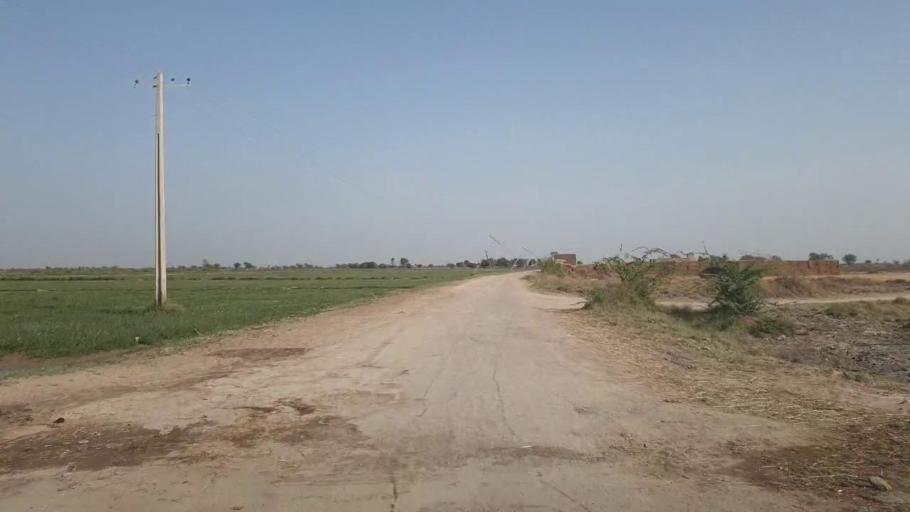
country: PK
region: Sindh
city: Dhoro Naro
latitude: 25.4630
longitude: 69.5573
